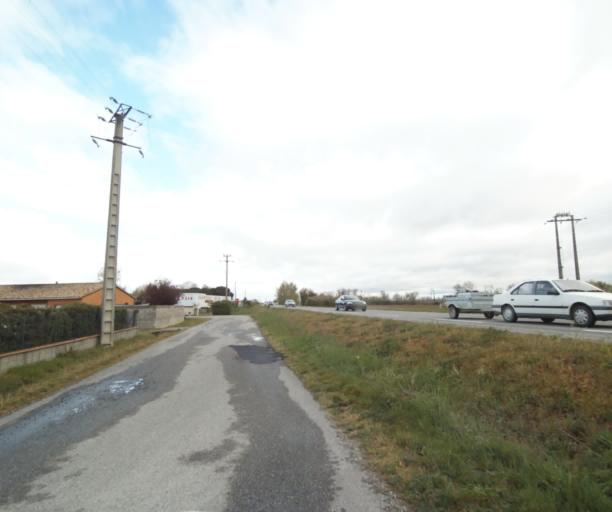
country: FR
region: Midi-Pyrenees
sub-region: Departement de l'Ariege
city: Saverdun
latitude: 43.2460
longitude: 1.5732
